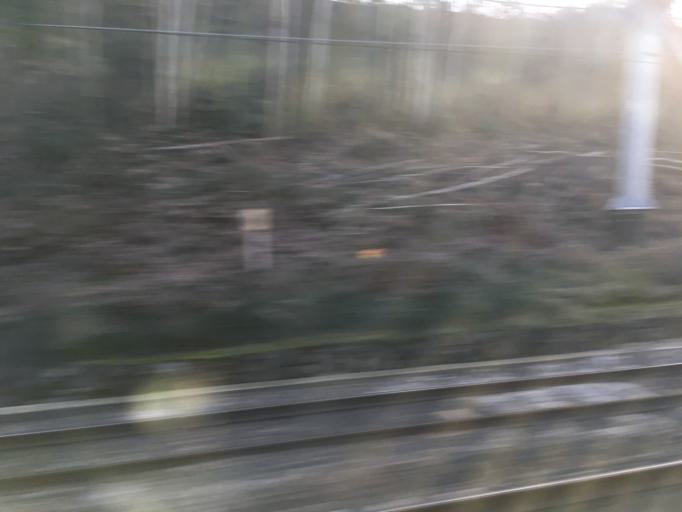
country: GB
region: England
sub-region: Oxfordshire
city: Goring
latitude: 51.5258
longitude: -1.1340
